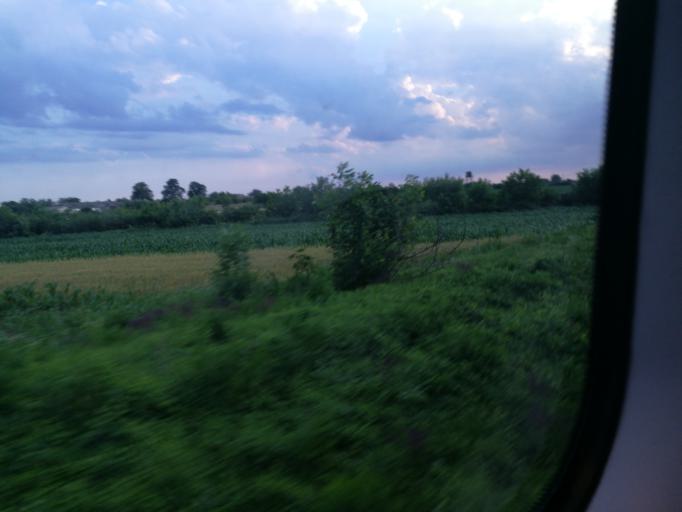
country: RO
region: Dambovita
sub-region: Comuna Titu
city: Titu
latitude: 44.6668
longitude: 25.5361
